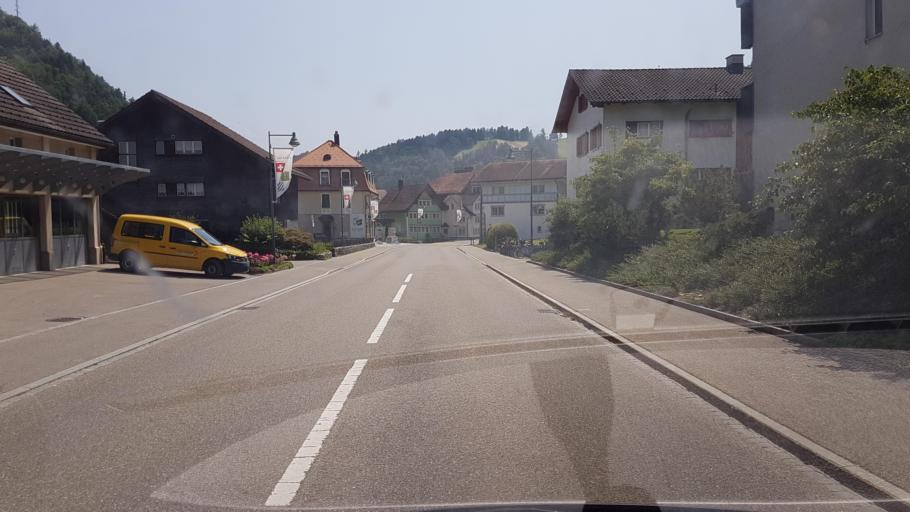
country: CH
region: Saint Gallen
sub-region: Wahlkreis Toggenburg
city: Mogelsberg
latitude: 47.3363
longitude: 9.1308
